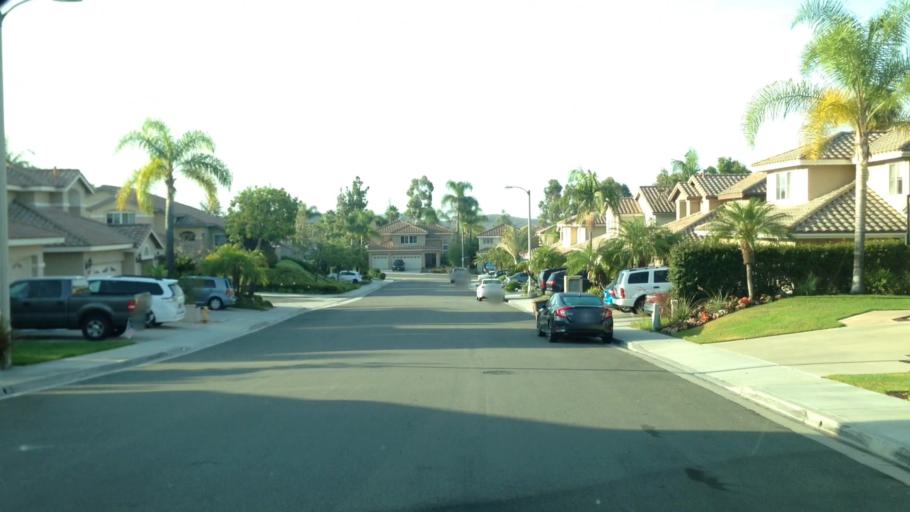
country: US
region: California
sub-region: Orange County
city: Rancho Santa Margarita
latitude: 33.6445
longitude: -117.6191
